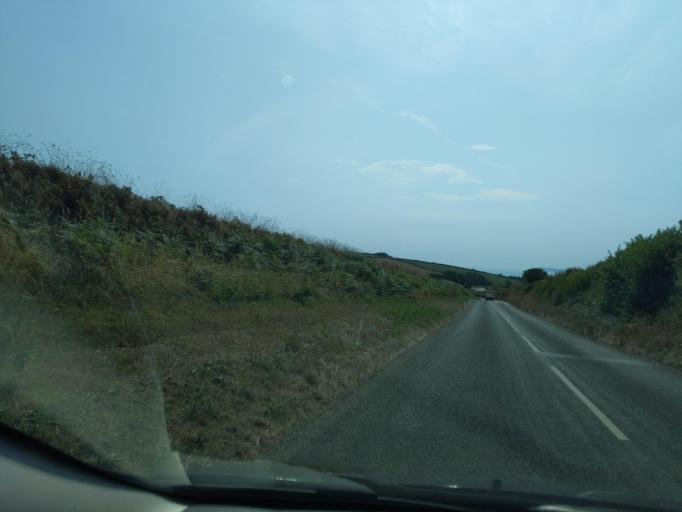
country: GB
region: England
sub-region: Cornwall
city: Fowey
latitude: 50.3491
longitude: -4.6146
